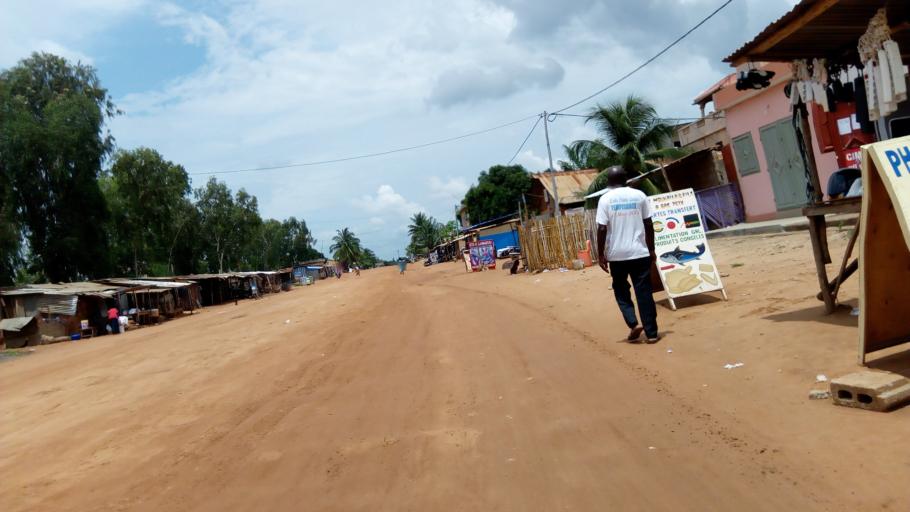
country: TG
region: Maritime
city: Lome
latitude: 6.2261
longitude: 1.1603
